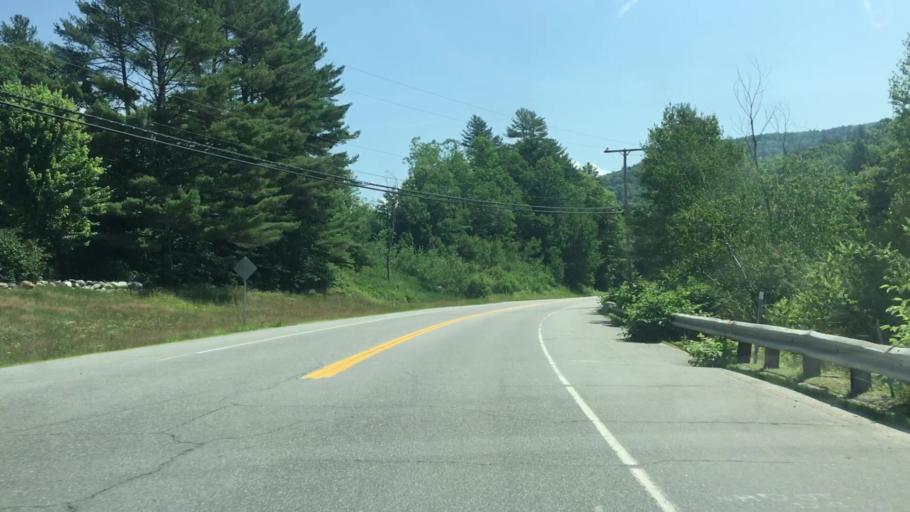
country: US
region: New Hampshire
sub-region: Sullivan County
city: Newport
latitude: 43.4155
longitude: -72.1843
